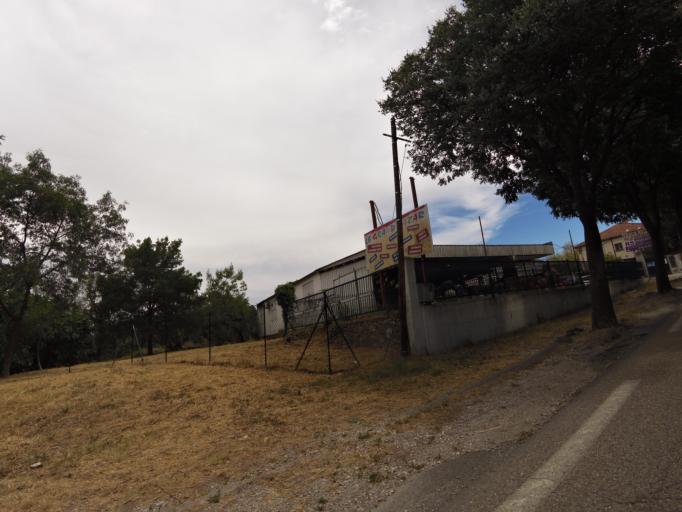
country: FR
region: Languedoc-Roussillon
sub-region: Departement du Gard
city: Quissac
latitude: 43.9114
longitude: 3.9995
